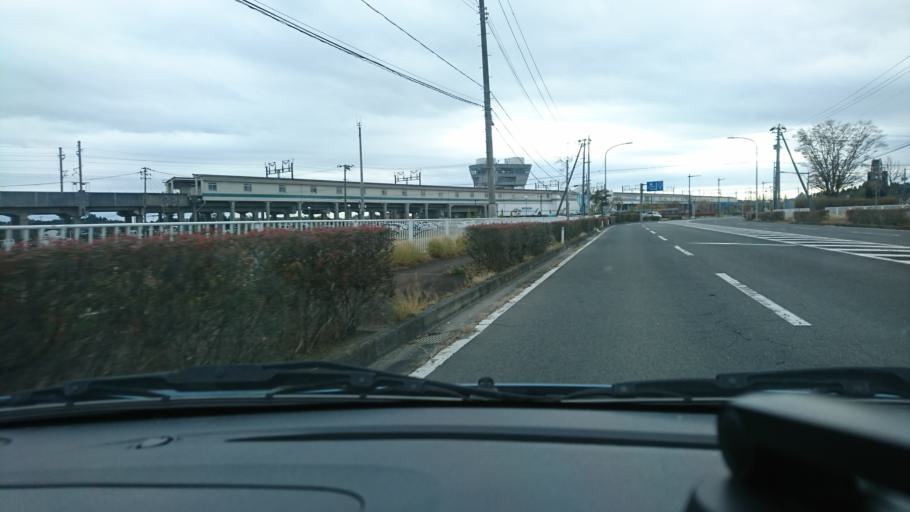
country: JP
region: Iwate
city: Ichinoseki
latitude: 38.7514
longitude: 141.0715
